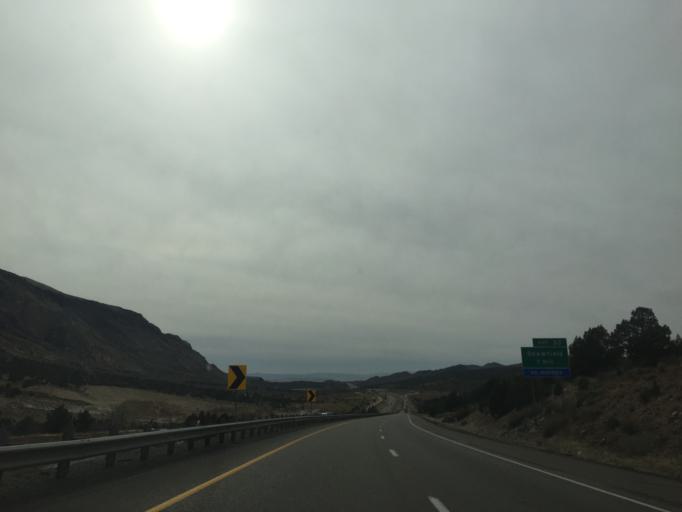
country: US
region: Utah
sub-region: Washington County
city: Toquerville
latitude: 37.3778
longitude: -113.2494
